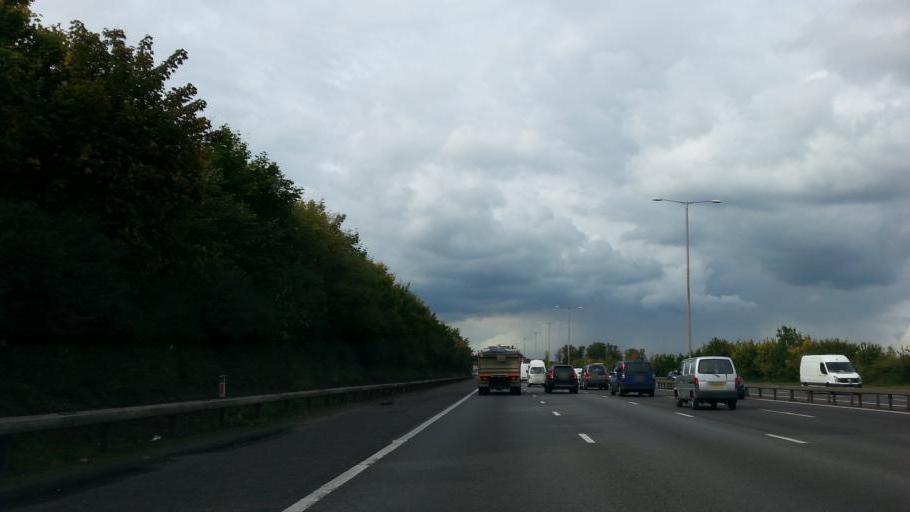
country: GB
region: England
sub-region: Greater London
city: Uxbridge
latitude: 51.5328
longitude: -0.4997
